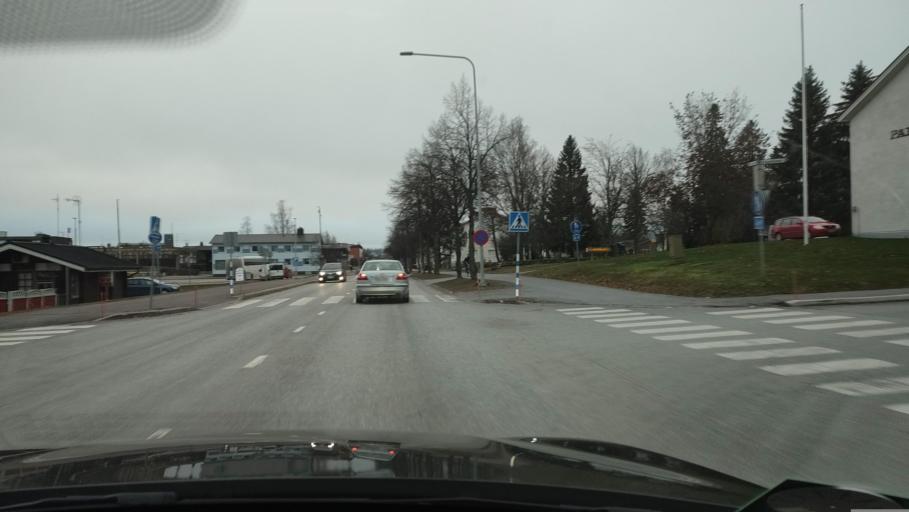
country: FI
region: Southern Ostrobothnia
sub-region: Suupohja
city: Kauhajoki
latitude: 62.4262
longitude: 22.1770
